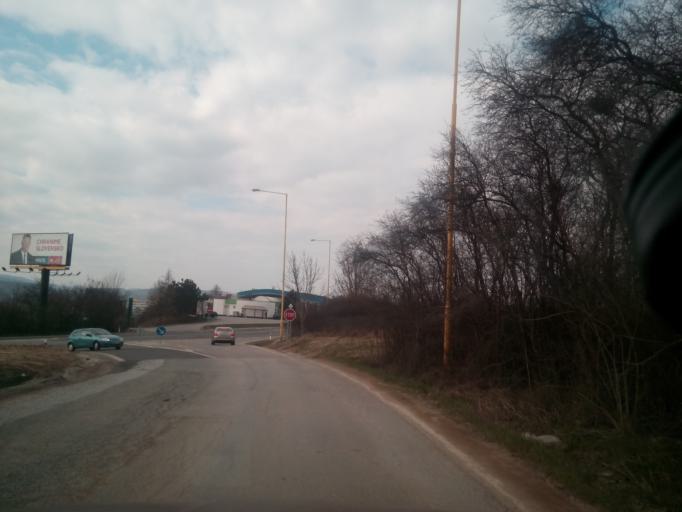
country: SK
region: Kosicky
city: Kosice
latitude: 48.7237
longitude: 21.2937
